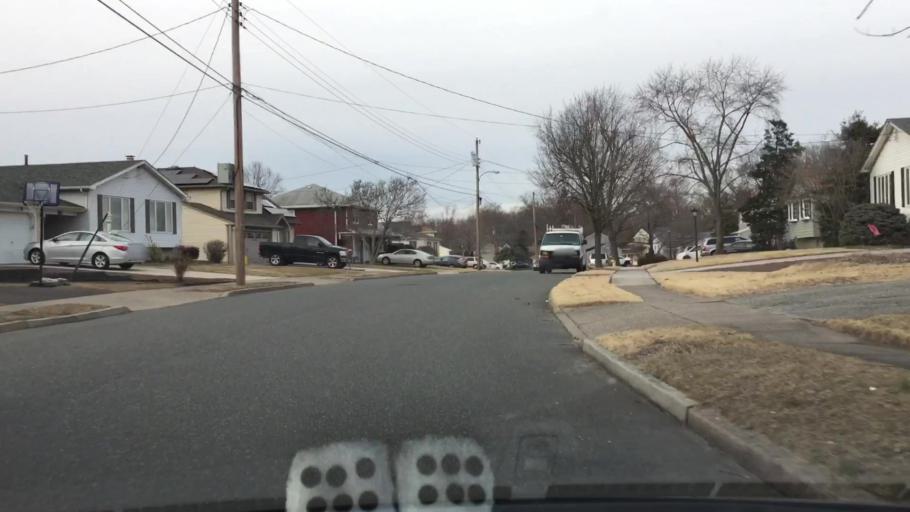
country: US
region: New Jersey
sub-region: Gloucester County
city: Turnersville
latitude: 39.7669
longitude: -75.0557
